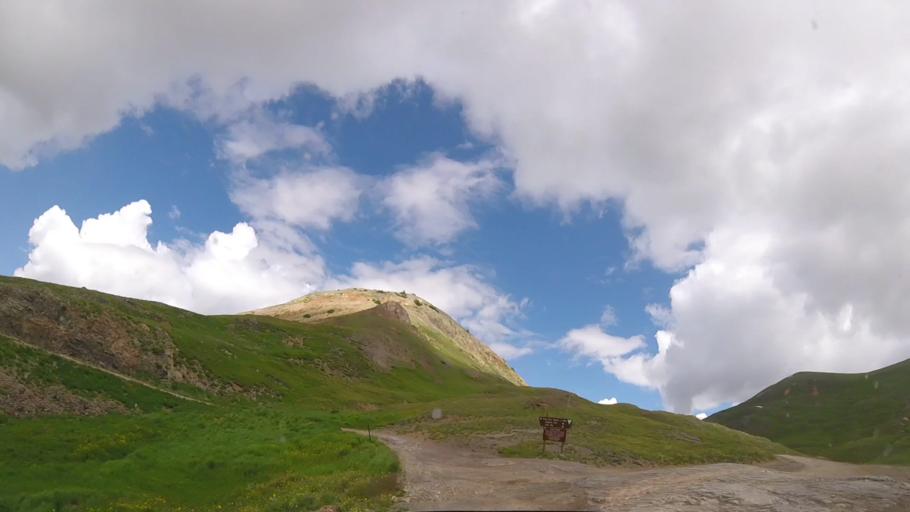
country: US
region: Colorado
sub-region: Ouray County
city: Ouray
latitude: 37.9488
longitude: -107.5762
